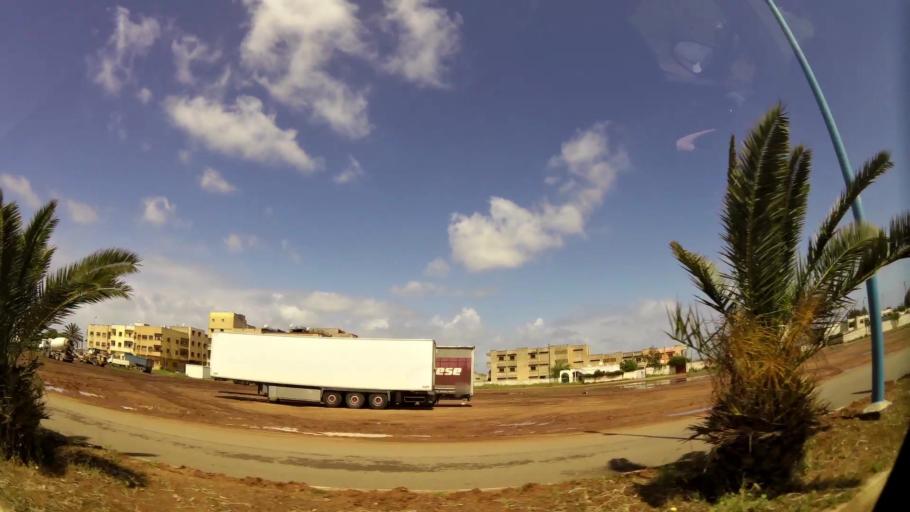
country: MA
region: Grand Casablanca
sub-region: Mediouna
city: Tit Mellil
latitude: 33.6366
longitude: -7.4585
